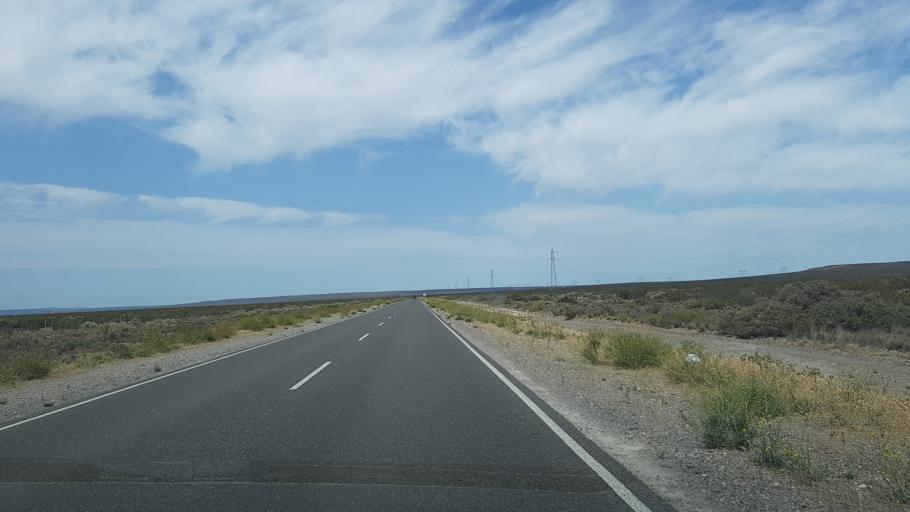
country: AR
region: Neuquen
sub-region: Departamento de Picun Leufu
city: Picun Leufu
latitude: -39.6808
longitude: -69.4607
